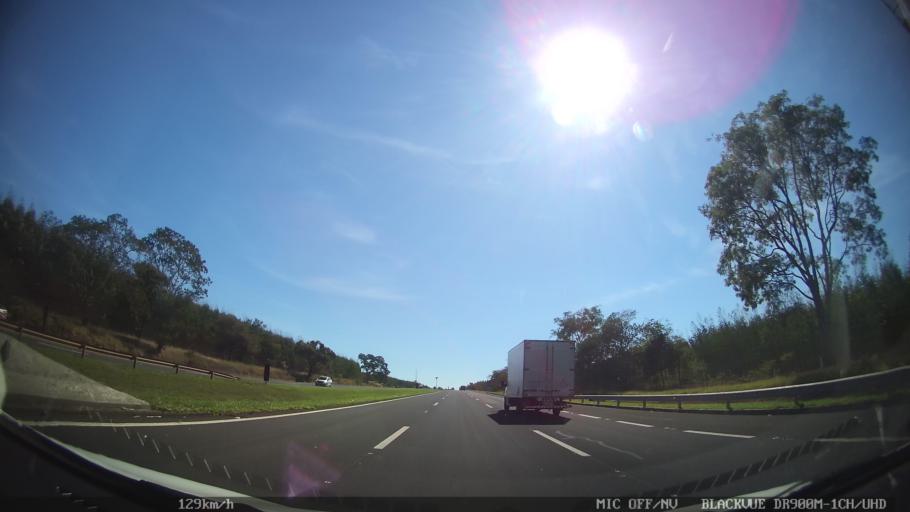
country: BR
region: Sao Paulo
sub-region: Sao Simao
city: Sao Simao
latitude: -21.5717
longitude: -47.6308
